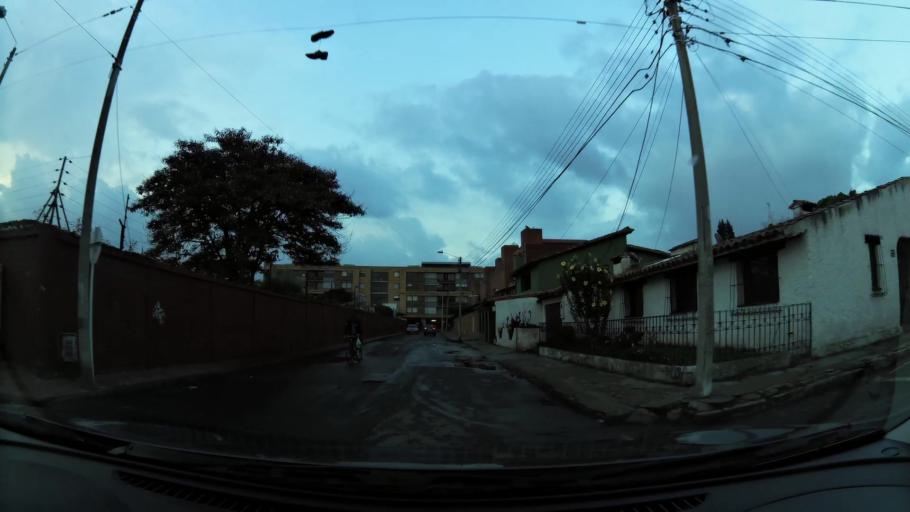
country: CO
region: Cundinamarca
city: Chia
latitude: 4.8589
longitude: -74.0562
